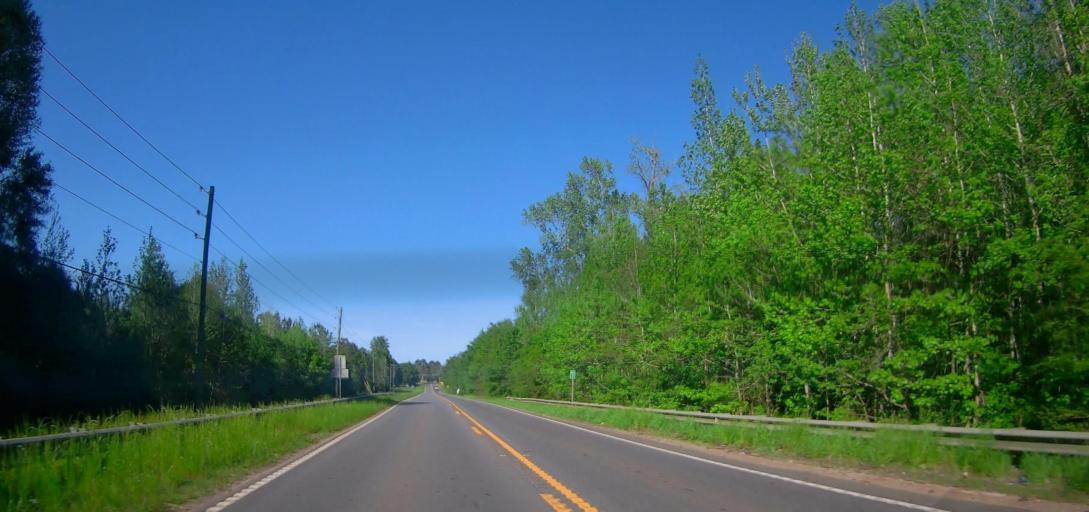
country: US
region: Georgia
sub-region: Houston County
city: Perry
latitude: 32.4517
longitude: -83.6236
